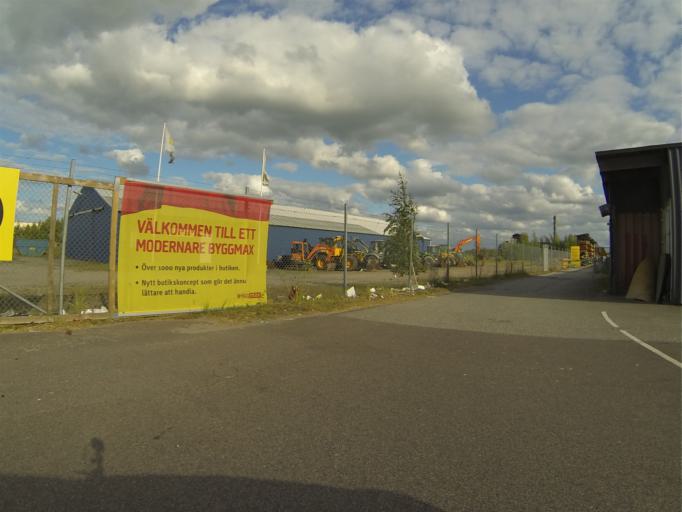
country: SE
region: Skane
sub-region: Staffanstorps Kommun
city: Staffanstorp
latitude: 55.6515
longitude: 13.2287
